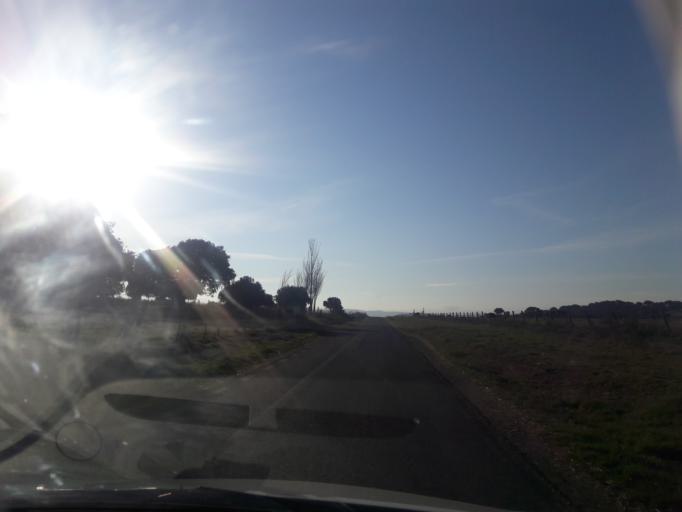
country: ES
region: Castille and Leon
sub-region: Provincia de Salamanca
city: Montejo
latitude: 40.6273
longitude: -5.6167
